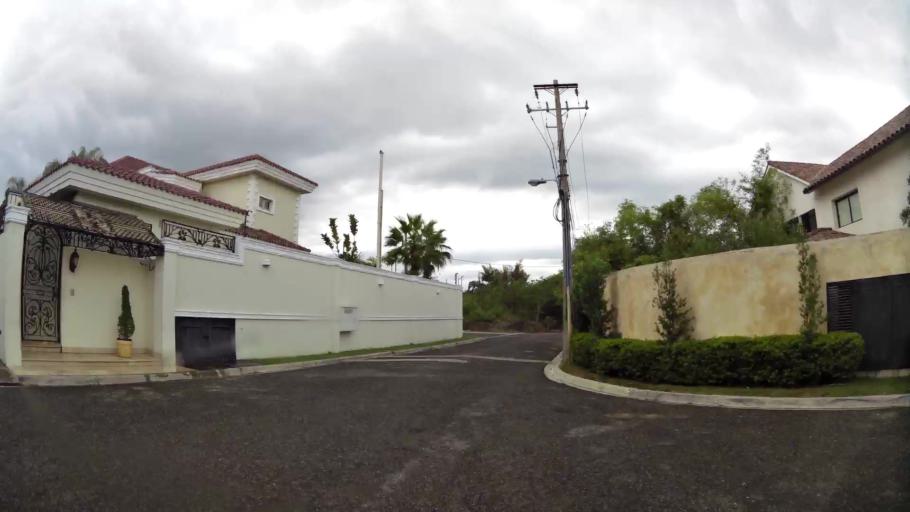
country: DO
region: Nacional
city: La Agustina
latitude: 18.5114
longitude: -69.9404
